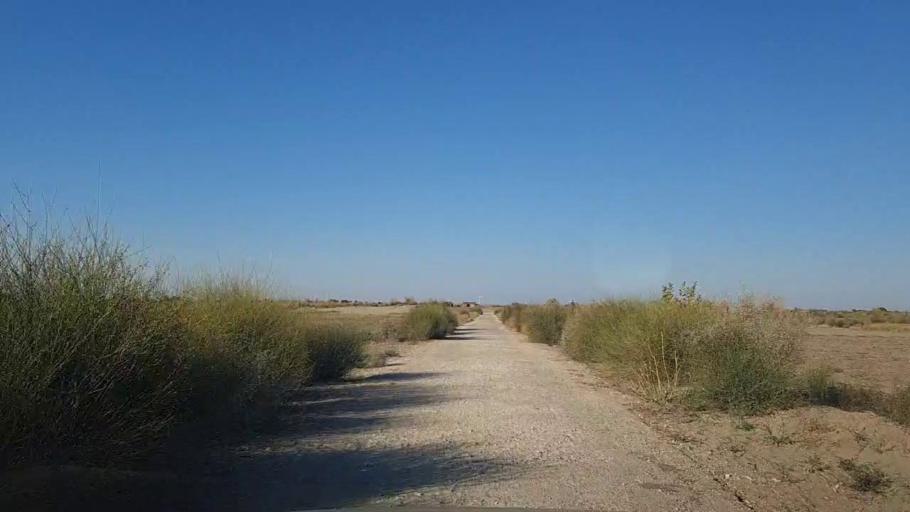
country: PK
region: Sindh
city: Khadro
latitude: 26.2450
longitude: 68.8629
